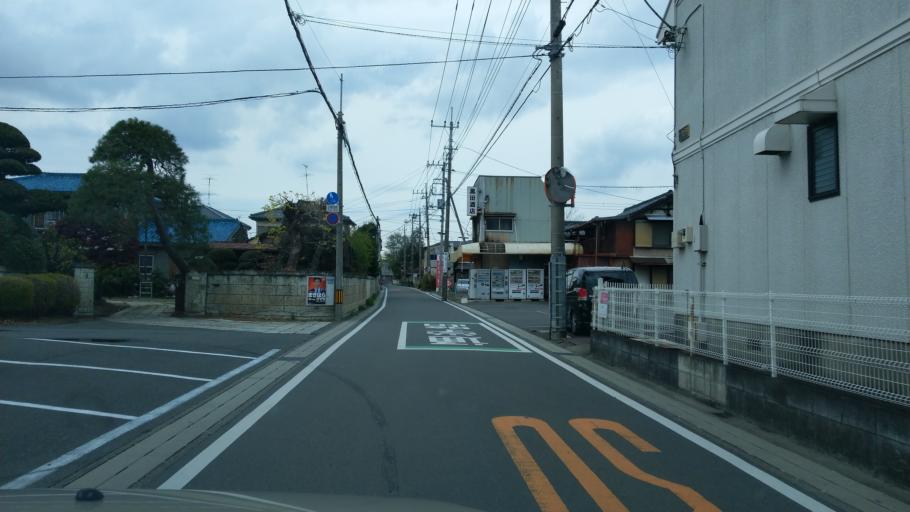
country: JP
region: Saitama
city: Yono
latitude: 35.9086
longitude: 139.5921
